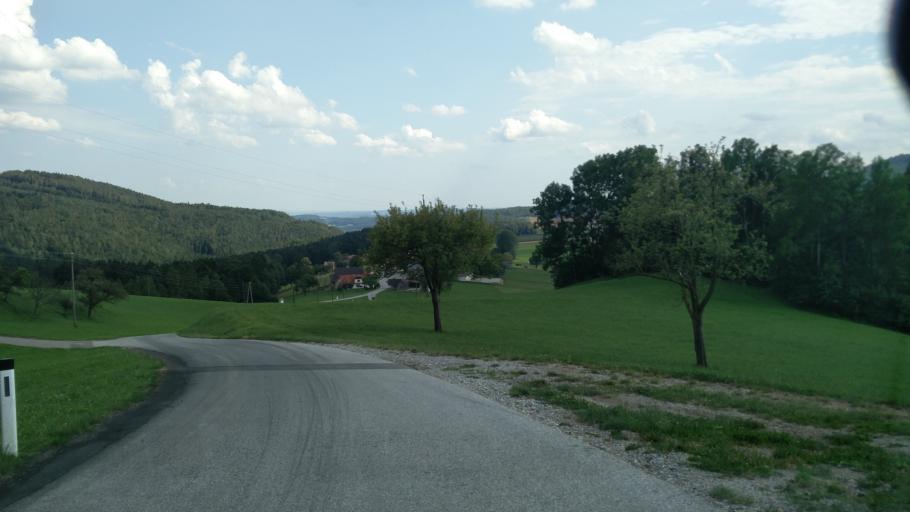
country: AT
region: Styria
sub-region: Politischer Bezirk Weiz
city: Naas
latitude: 47.2515
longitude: 15.6019
